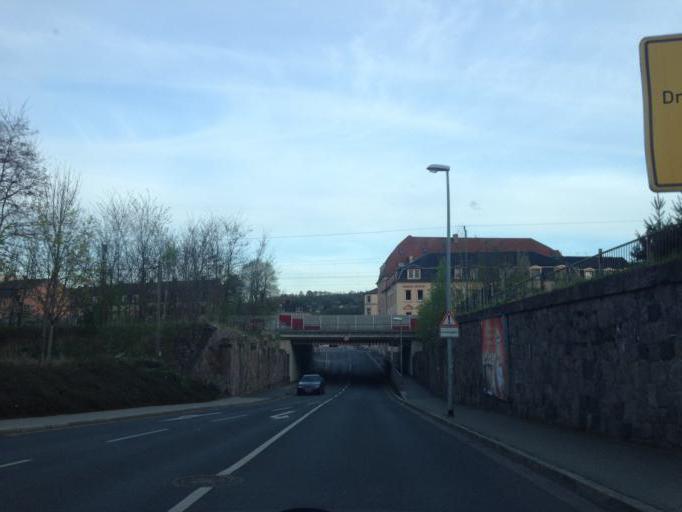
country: DE
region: Saxony
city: Freital
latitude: 51.0150
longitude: 13.6628
